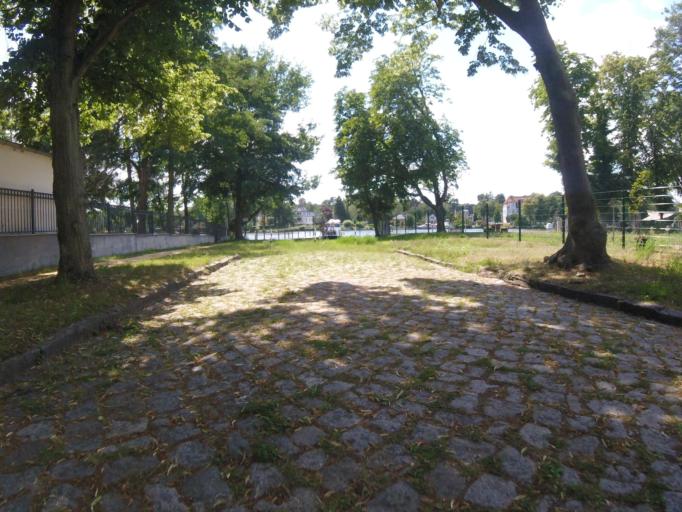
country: DE
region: Brandenburg
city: Wildau
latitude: 52.3382
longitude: 13.6411
